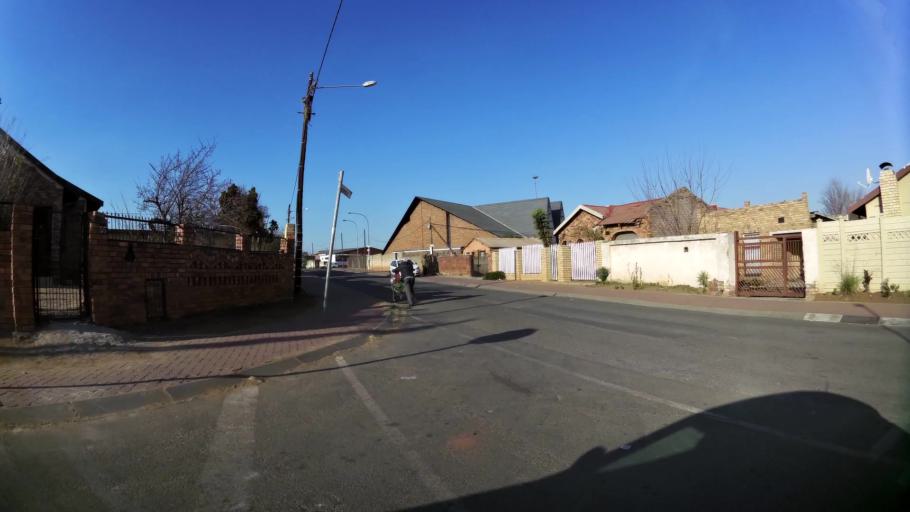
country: ZA
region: Gauteng
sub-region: City of Johannesburg Metropolitan Municipality
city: Soweto
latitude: -26.2619
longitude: 27.8819
